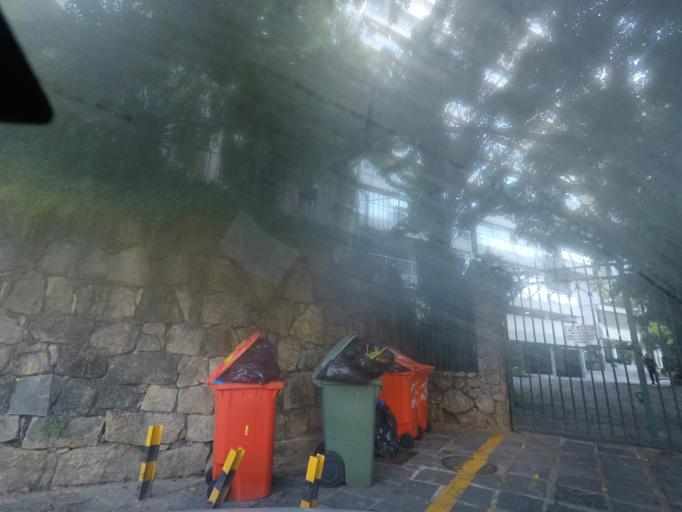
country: BR
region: Rio de Janeiro
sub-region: Rio De Janeiro
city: Rio de Janeiro
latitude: -22.9626
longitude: -43.2014
